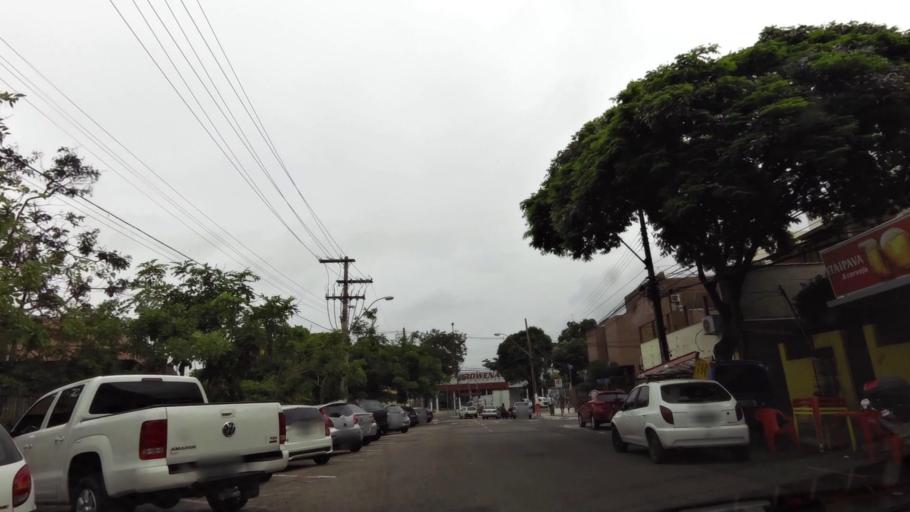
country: BR
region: Espirito Santo
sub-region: Vila Velha
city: Vila Velha
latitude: -20.3156
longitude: -40.2993
